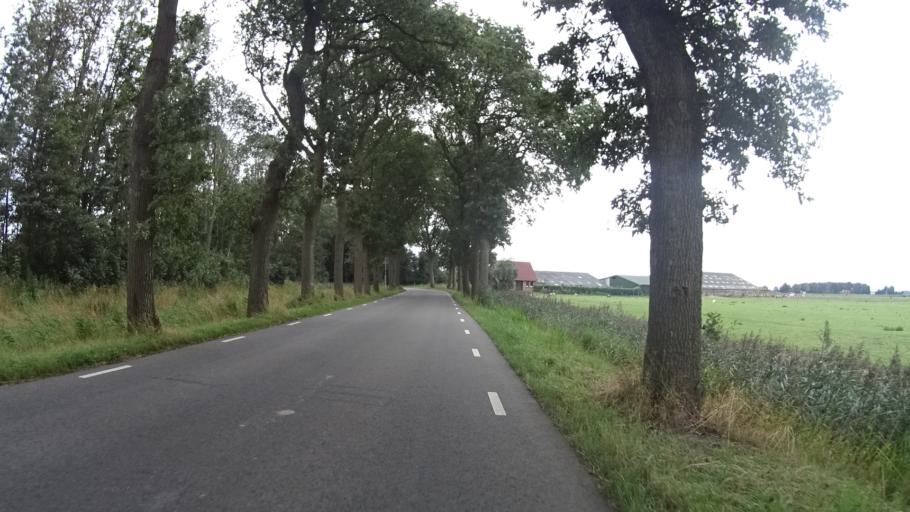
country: NL
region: Groningen
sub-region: Gemeente Slochteren
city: Slochteren
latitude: 53.2030
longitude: 6.8378
